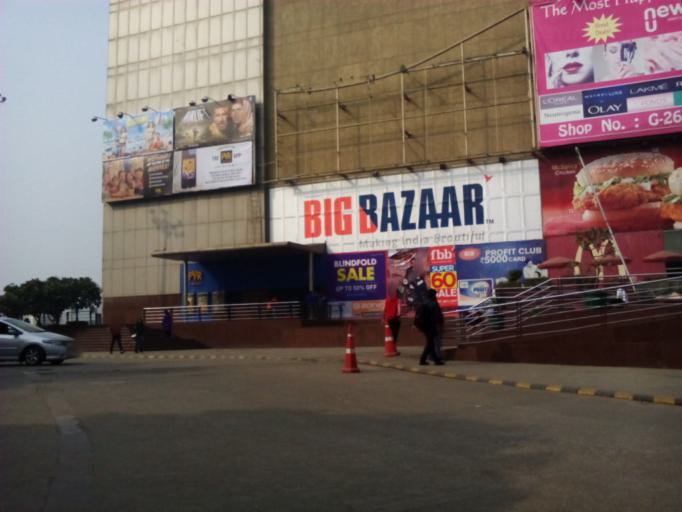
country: IN
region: Uttar Pradesh
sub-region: Gautam Buddha Nagar
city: Noida
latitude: 28.6411
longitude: 77.3177
